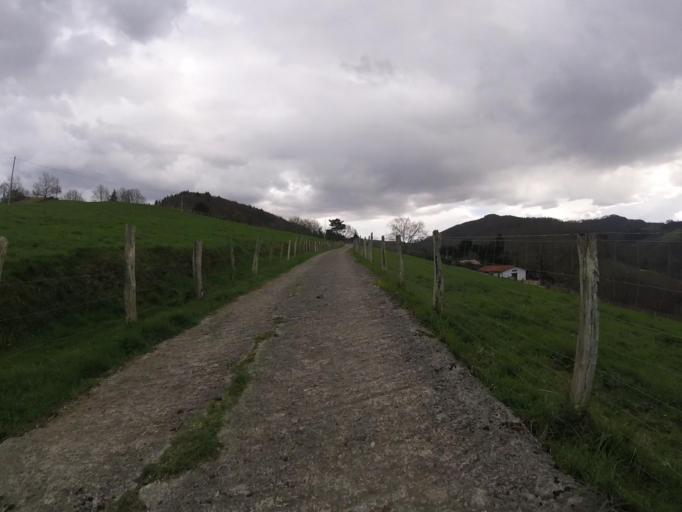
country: ES
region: Basque Country
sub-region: Provincia de Guipuzcoa
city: Errenteria
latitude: 43.2777
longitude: -1.8625
